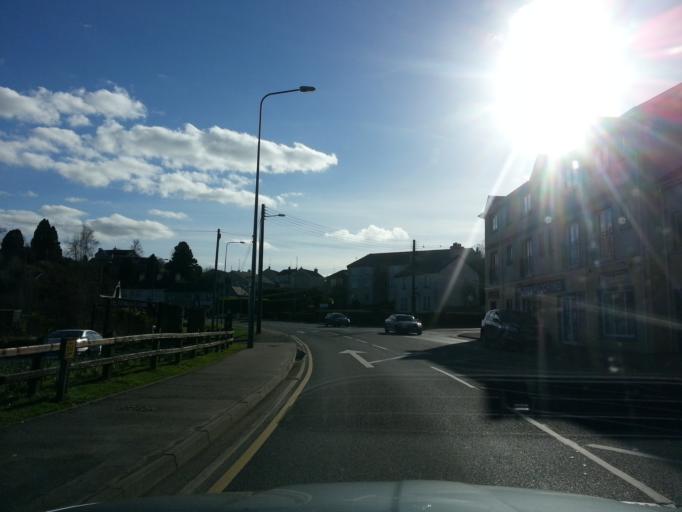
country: GB
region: Northern Ireland
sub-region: Fermanagh District
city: Enniskillen
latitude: 54.3447
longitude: -7.6499
